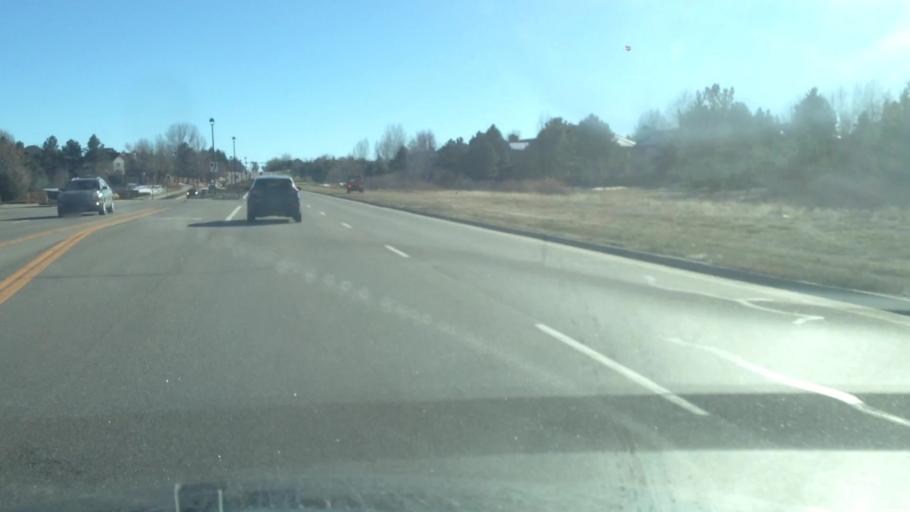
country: US
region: Colorado
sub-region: Douglas County
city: Stonegate
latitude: 39.5295
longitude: -104.7933
